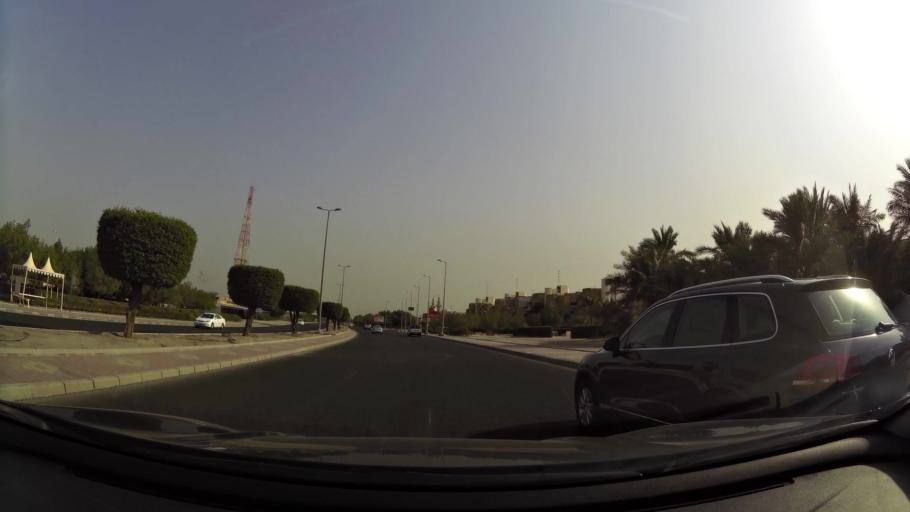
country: KW
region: Mubarak al Kabir
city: Sabah as Salim
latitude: 29.2533
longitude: 48.0633
